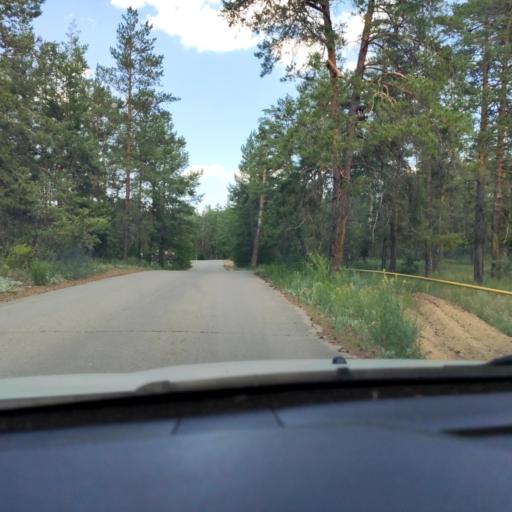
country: RU
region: Samara
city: Pribrezhnyy
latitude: 53.4772
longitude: 49.8220
